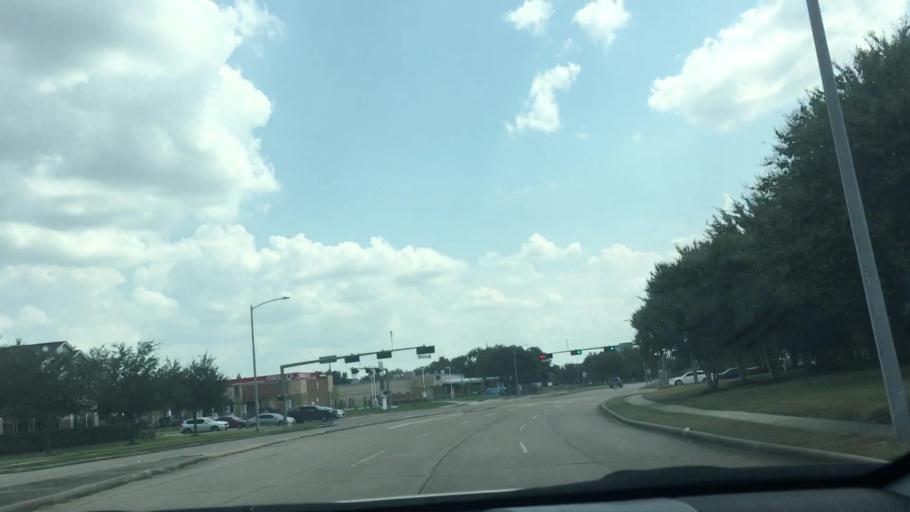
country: US
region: Texas
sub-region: Fort Bend County
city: Mission Bend
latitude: 29.7302
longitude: -95.6360
